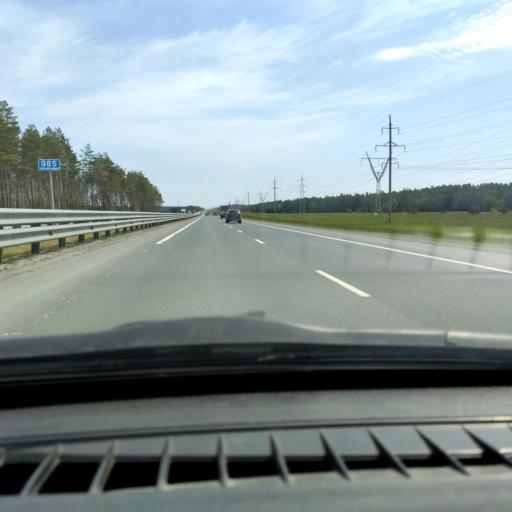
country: RU
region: Samara
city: Povolzhskiy
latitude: 53.5147
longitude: 49.6635
